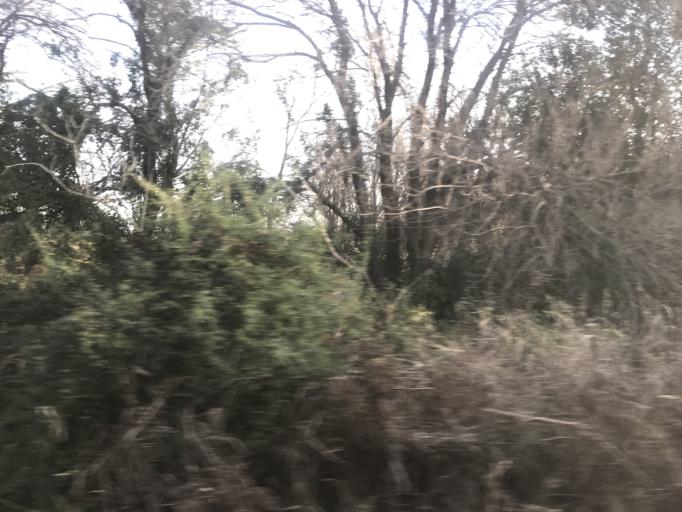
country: AR
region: Cordoba
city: Malvinas Argentinas
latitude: -31.4688
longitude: -64.0992
